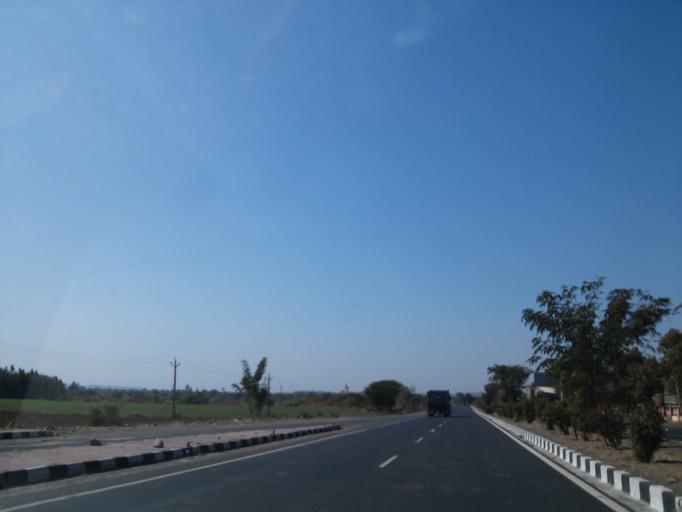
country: IN
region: Gujarat
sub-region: Sabar Kantha
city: Modasa
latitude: 23.5997
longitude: 73.2056
